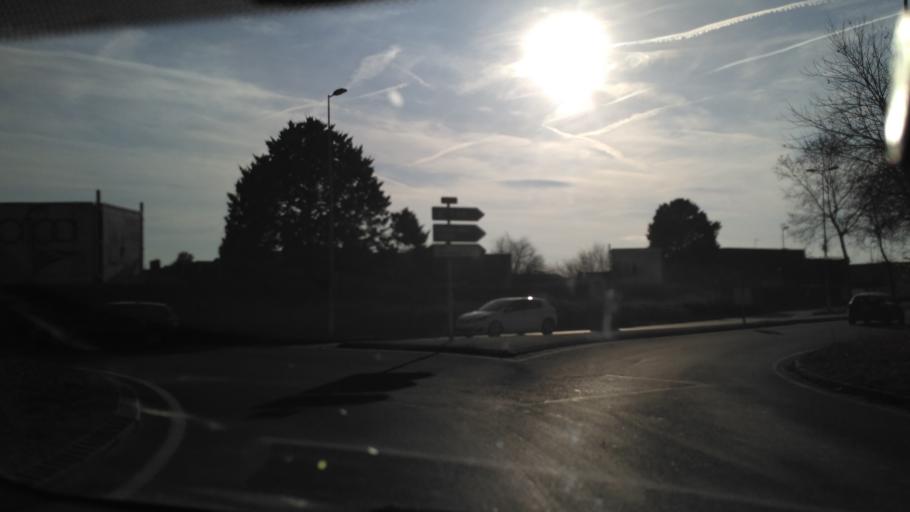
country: FR
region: Rhone-Alpes
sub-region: Departement de la Drome
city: Genissieux
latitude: 45.0541
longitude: 5.0887
